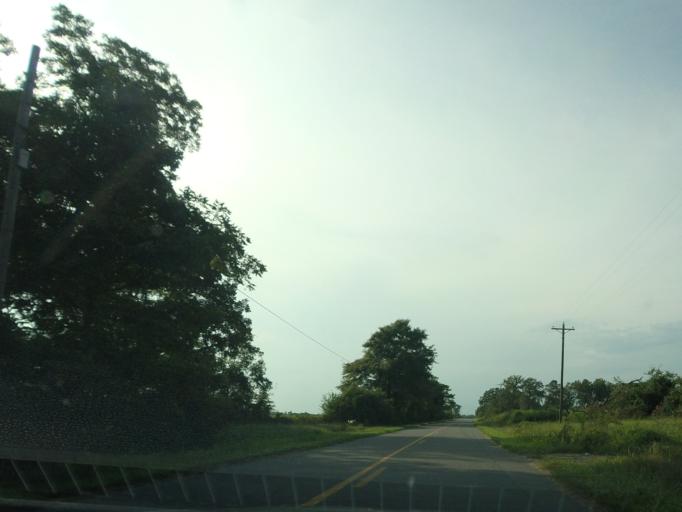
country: US
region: Georgia
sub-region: Bleckley County
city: Cochran
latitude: 32.5020
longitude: -83.2994
